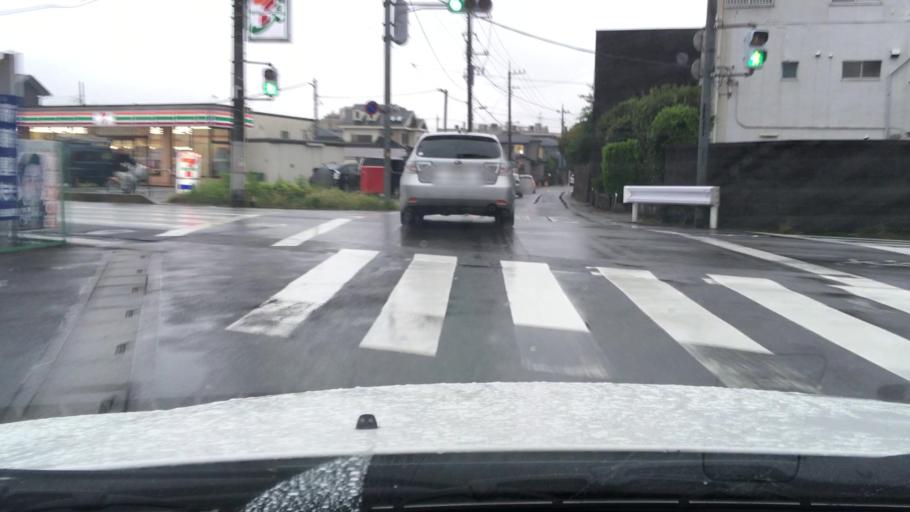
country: JP
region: Saitama
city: Yono
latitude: 35.9064
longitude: 139.6078
